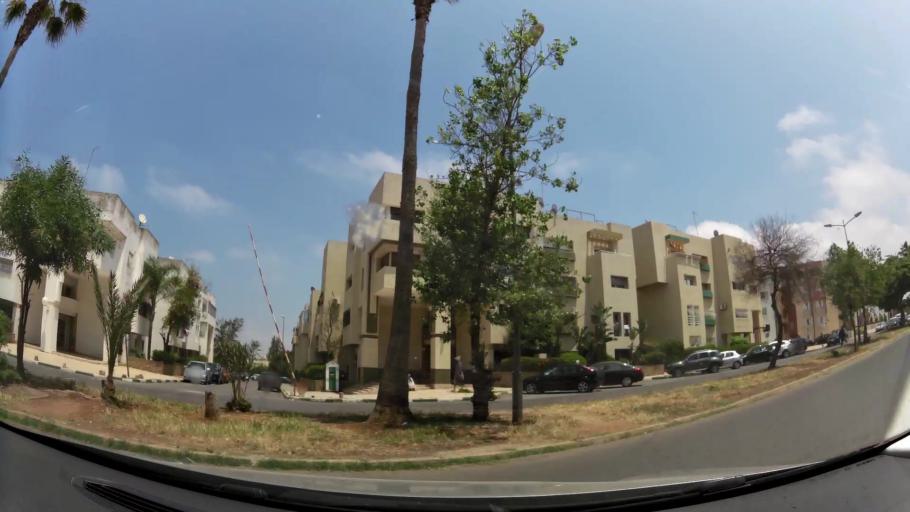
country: MA
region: Rabat-Sale-Zemmour-Zaer
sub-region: Skhirate-Temara
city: Temara
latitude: 33.9679
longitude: -6.9040
